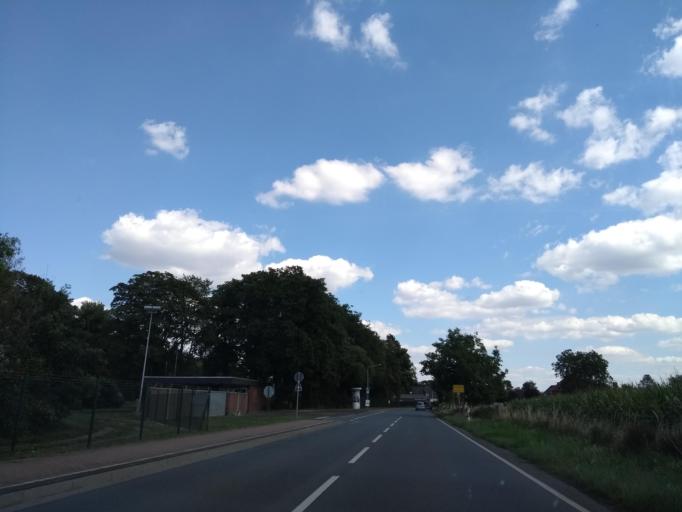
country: DE
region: Lower Saxony
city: Wunstorf
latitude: 52.4528
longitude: 9.4147
